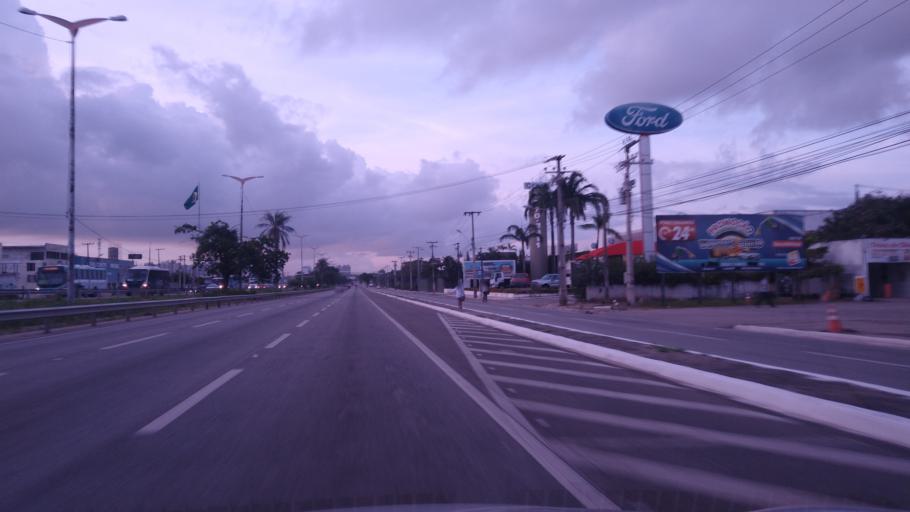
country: BR
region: Ceara
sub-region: Fortaleza
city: Fortaleza
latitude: -3.7893
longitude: -38.5103
